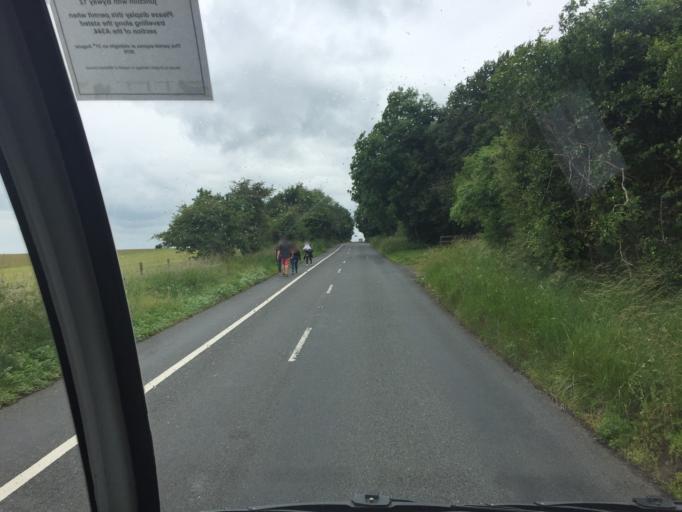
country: GB
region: England
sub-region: Wiltshire
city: Durnford
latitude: 51.1824
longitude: -1.8387
